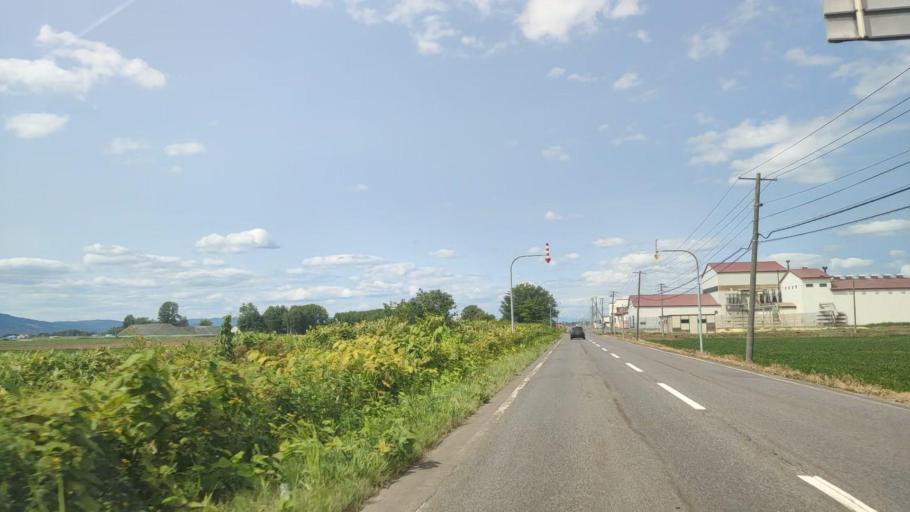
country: JP
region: Hokkaido
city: Nayoro
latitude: 44.2022
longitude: 142.4158
